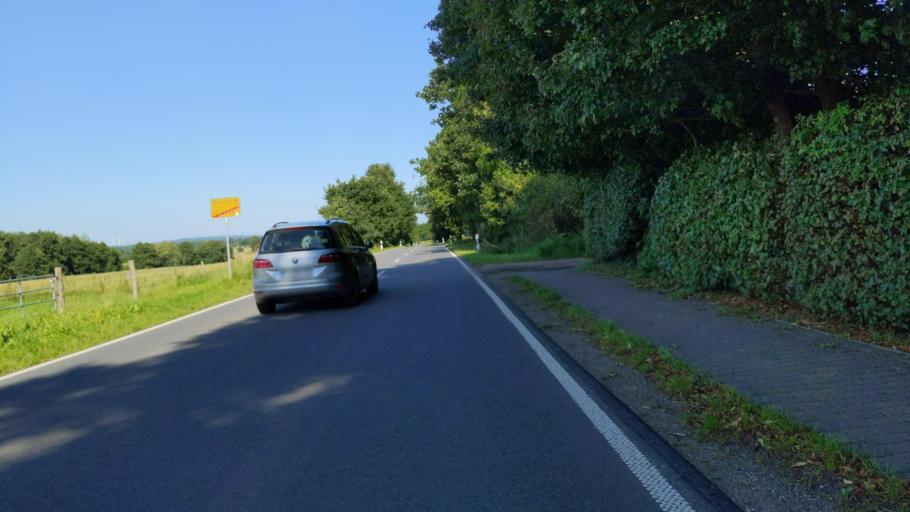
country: DE
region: Schleswig-Holstein
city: Stockelsdorf
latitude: 53.9528
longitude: 10.6262
